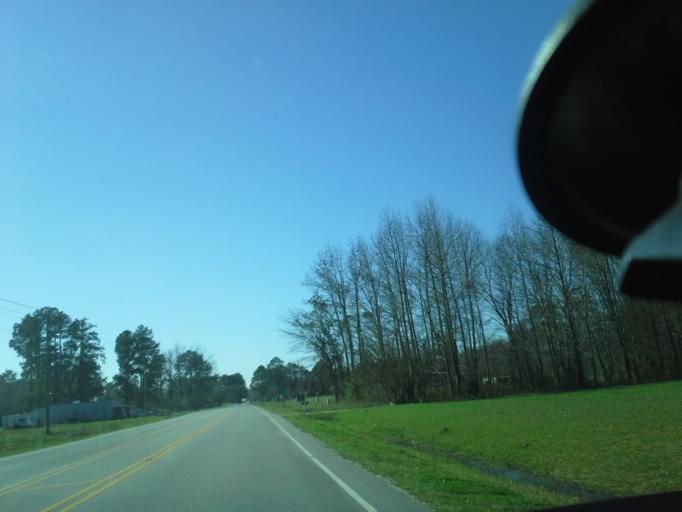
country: US
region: North Carolina
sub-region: Beaufort County
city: Belhaven
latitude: 35.5345
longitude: -76.7236
